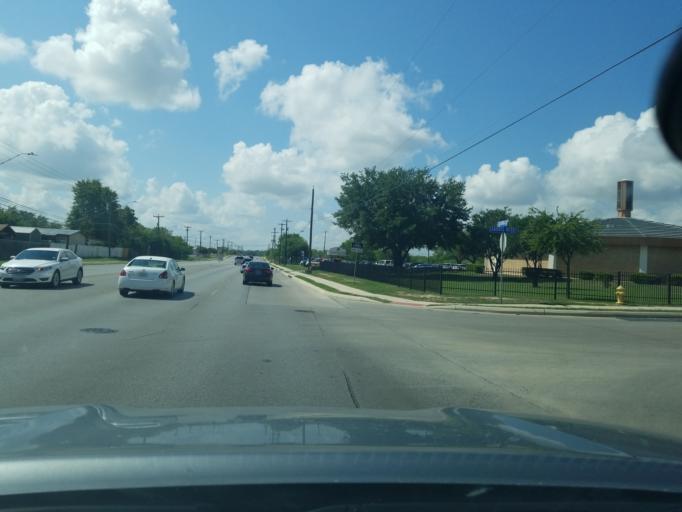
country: US
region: Texas
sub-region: Bexar County
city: San Antonio
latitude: 29.3428
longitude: -98.5343
